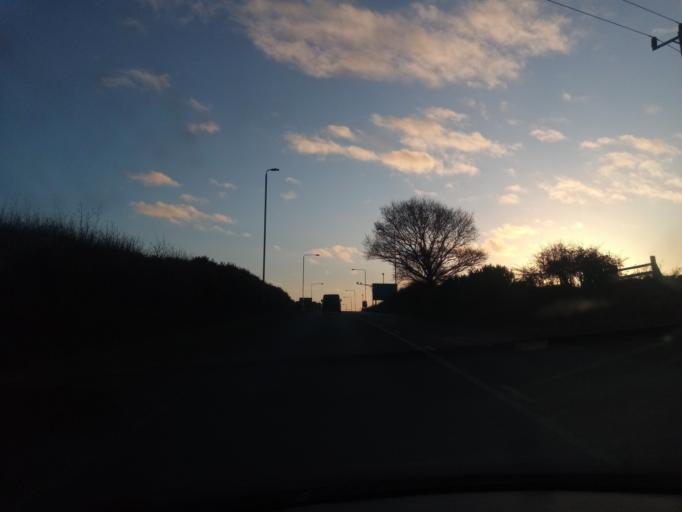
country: GB
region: England
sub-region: Nottinghamshire
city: Farnsfield
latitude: 53.0934
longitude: -1.0688
